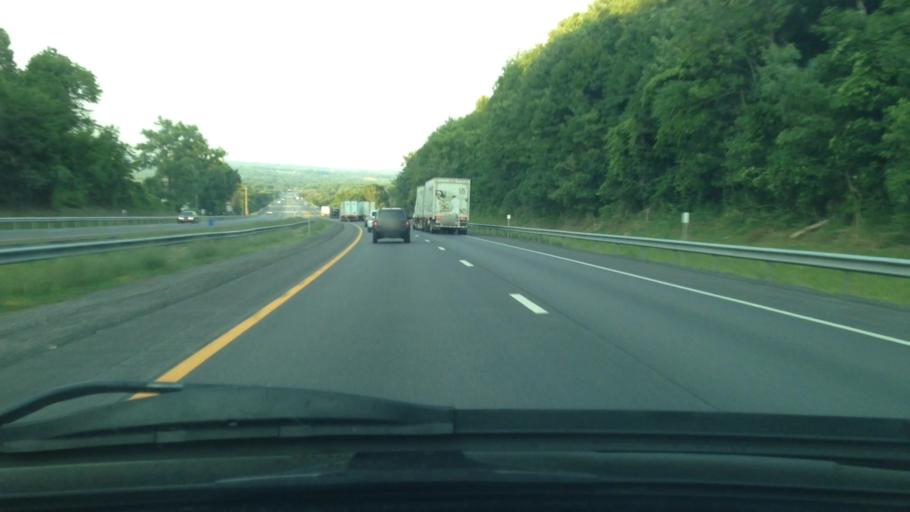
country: US
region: New York
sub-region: Oneida County
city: Whitesboro
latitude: 43.1280
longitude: -75.3066
